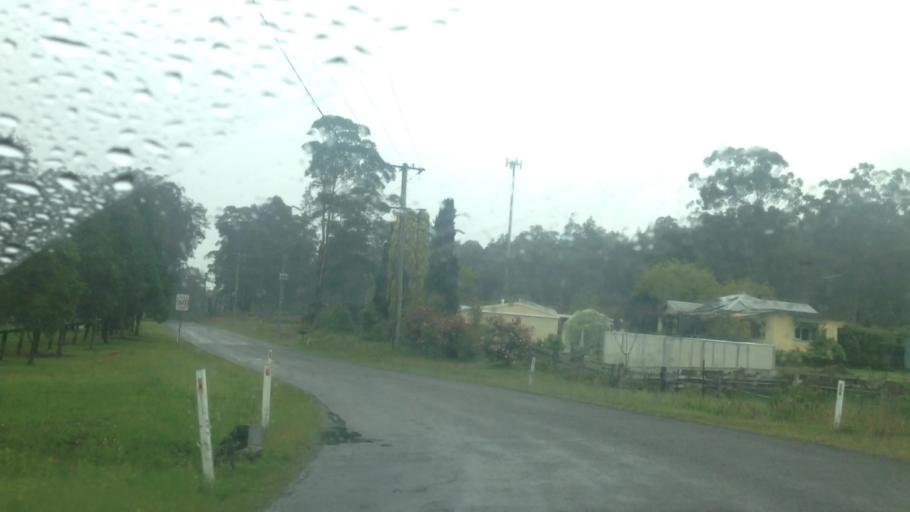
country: AU
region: New South Wales
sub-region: Wyong Shire
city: Little Jilliby
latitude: -33.1899
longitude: 151.3549
